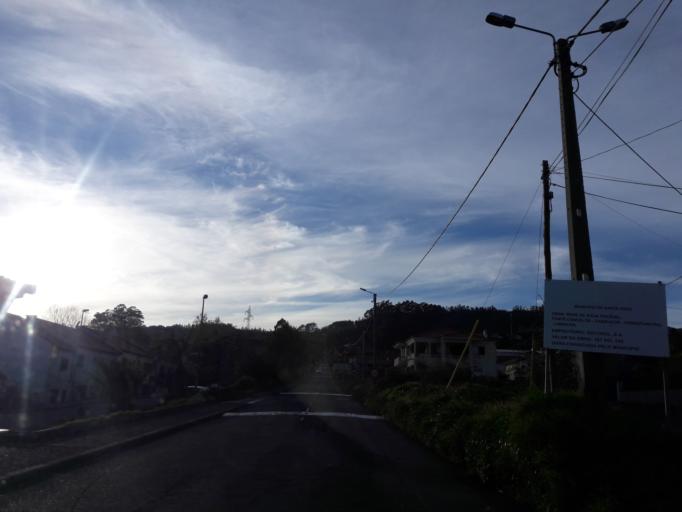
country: PT
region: Madeira
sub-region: Santa Cruz
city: Camacha
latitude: 32.6703
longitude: -16.8452
